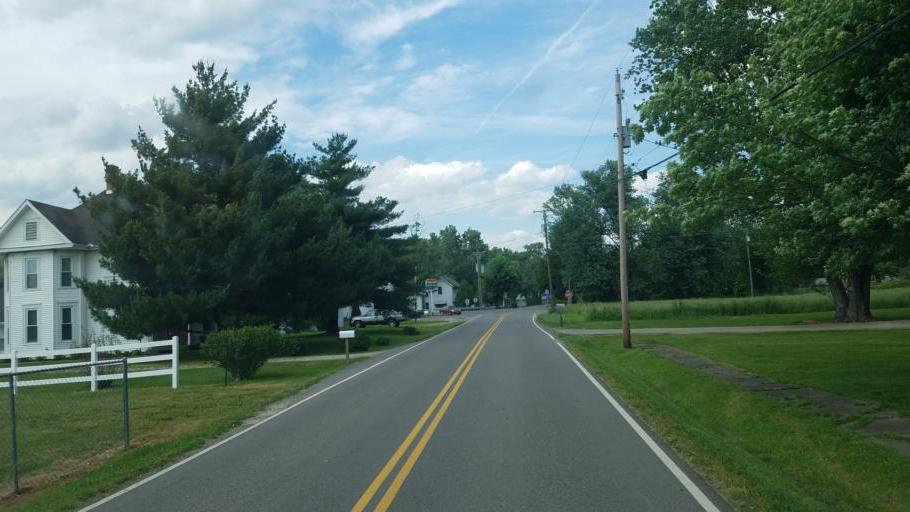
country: US
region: Ohio
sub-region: Meigs County
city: Pomeroy
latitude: 39.1251
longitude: -82.1343
